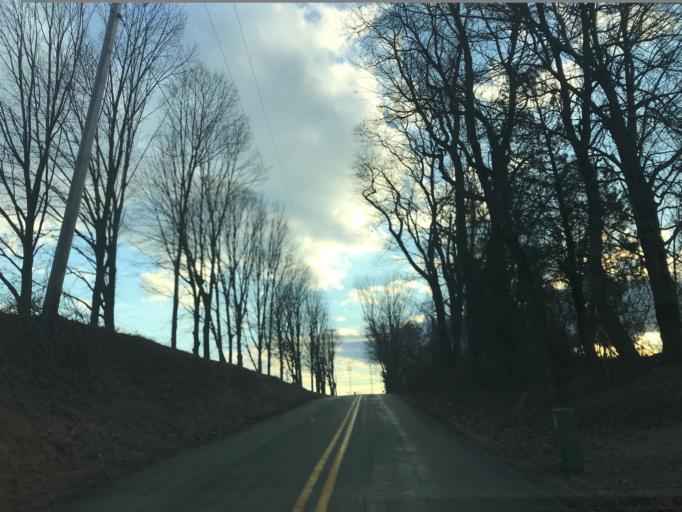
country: US
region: Maryland
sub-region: Harford County
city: Jarrettsville
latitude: 39.5985
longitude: -76.4379
